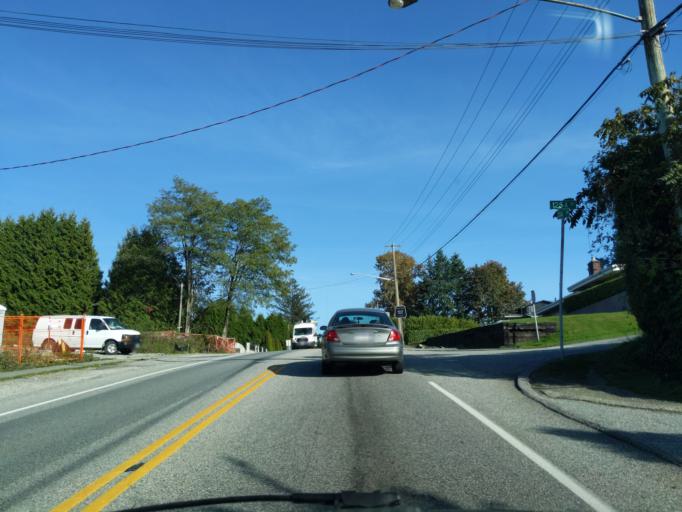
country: CA
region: British Columbia
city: New Westminster
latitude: 49.1917
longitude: -122.8743
